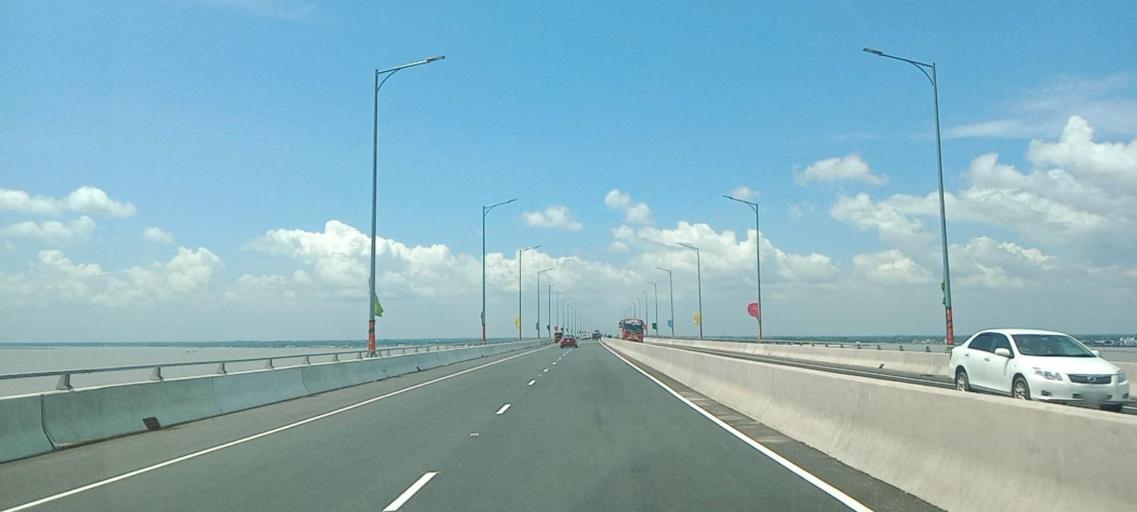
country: BD
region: Dhaka
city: Char Bhadrasan
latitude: 23.4452
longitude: 90.2612
